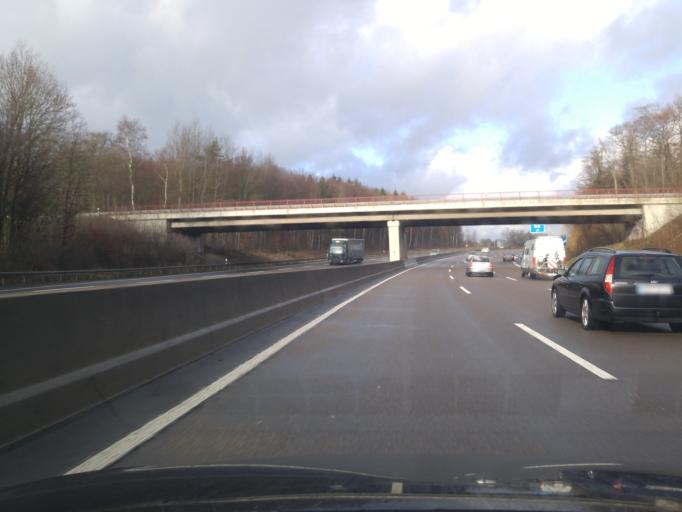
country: DE
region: Hesse
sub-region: Regierungsbezirk Kassel
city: Malsfeld
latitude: 51.0307
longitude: 9.4845
